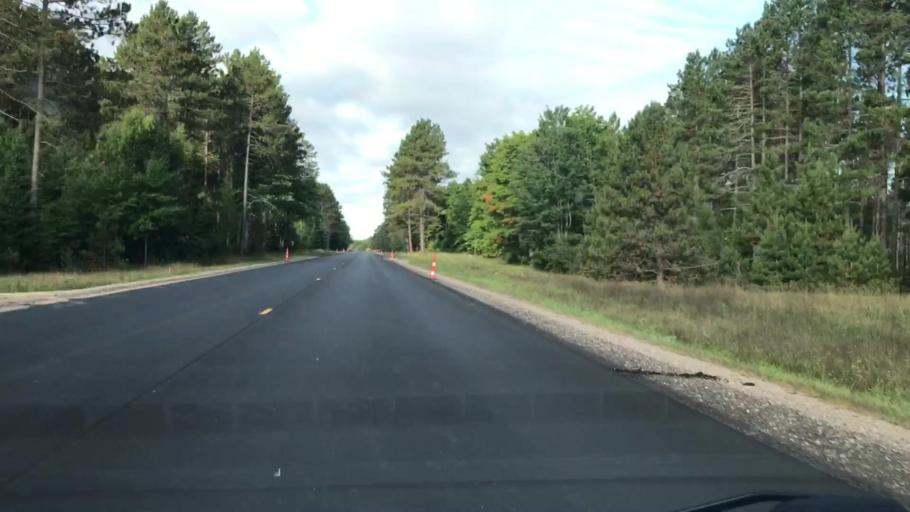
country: US
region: Michigan
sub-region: Luce County
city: Newberry
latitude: 46.3464
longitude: -85.0108
